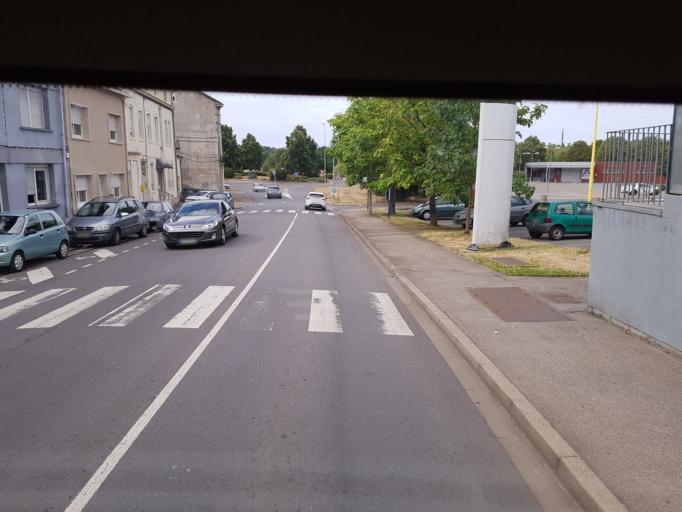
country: FR
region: Lorraine
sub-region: Departement de Meurthe-et-Moselle
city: Joeuf
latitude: 49.2234
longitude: 6.0068
